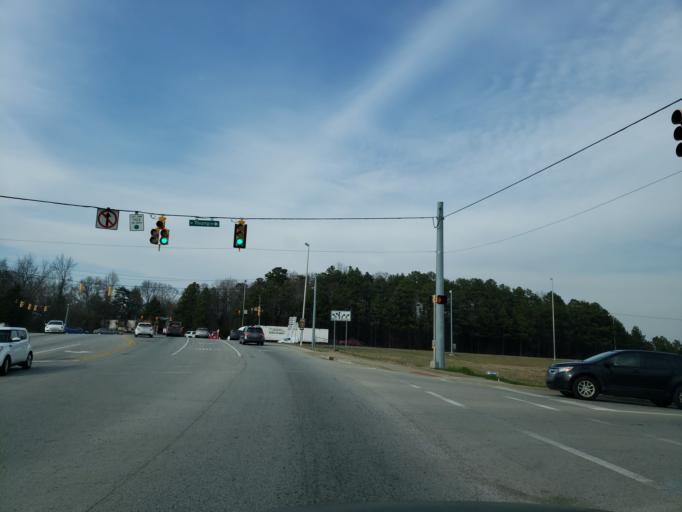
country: US
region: Tennessee
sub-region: Bradley County
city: South Cleveland
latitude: 35.1300
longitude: -84.8650
